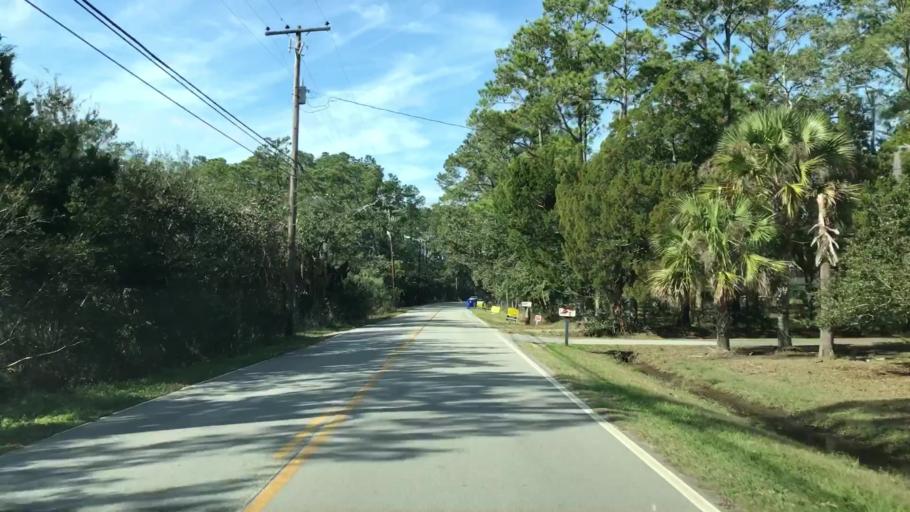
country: US
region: South Carolina
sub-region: Charleston County
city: Charleston
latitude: 32.7745
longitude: -80.0149
